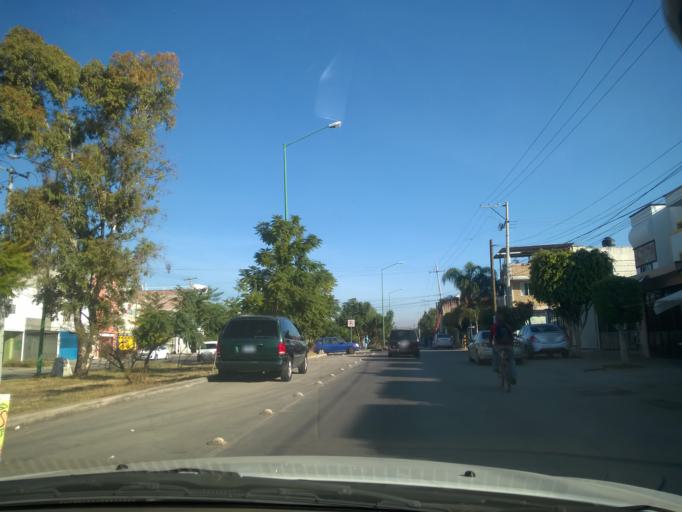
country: MX
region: Guanajuato
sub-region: Leon
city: San Jose de Duran (Los Troncoso)
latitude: 21.0873
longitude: -101.6429
